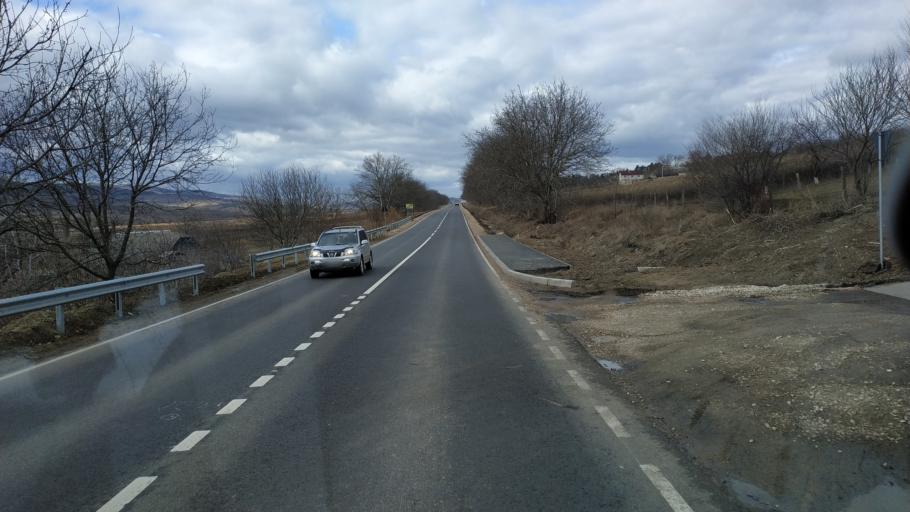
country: MD
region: Stinga Nistrului
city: Bucovat
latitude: 47.2034
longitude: 28.4273
